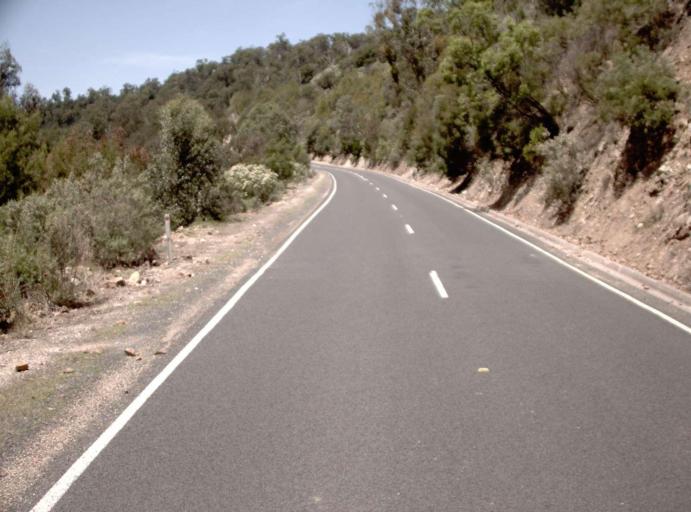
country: AU
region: Victoria
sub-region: East Gippsland
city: Lakes Entrance
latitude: -37.5542
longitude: 147.8786
